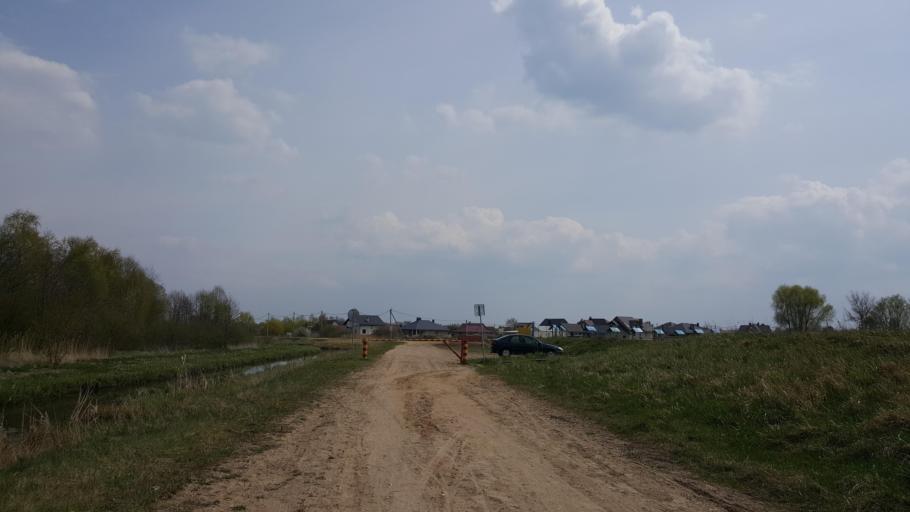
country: BY
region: Brest
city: Zhabinka
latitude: 52.2012
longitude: 23.9888
